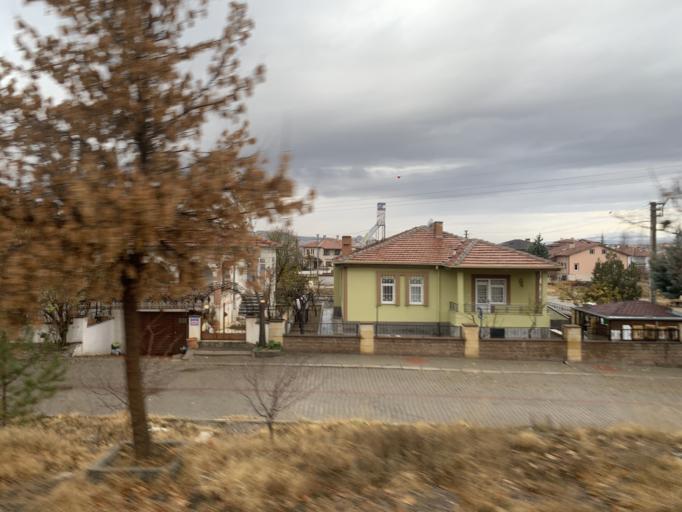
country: TR
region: Nevsehir
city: Avanos
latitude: 38.7104
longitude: 34.8580
